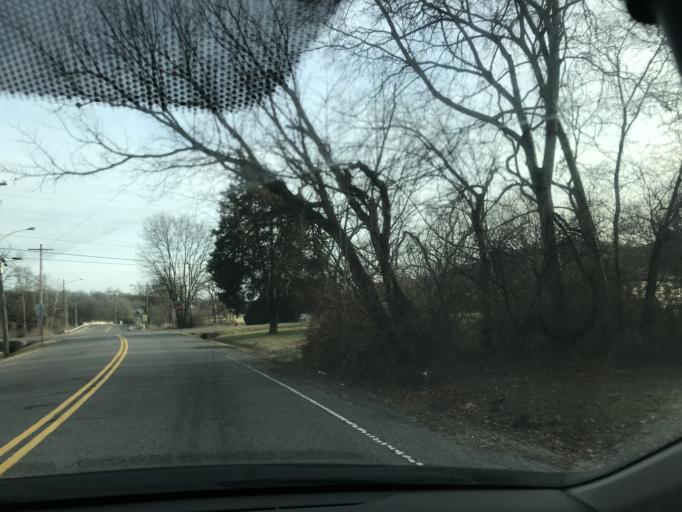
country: US
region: Tennessee
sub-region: Davidson County
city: Nashville
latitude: 36.2137
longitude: -86.8261
